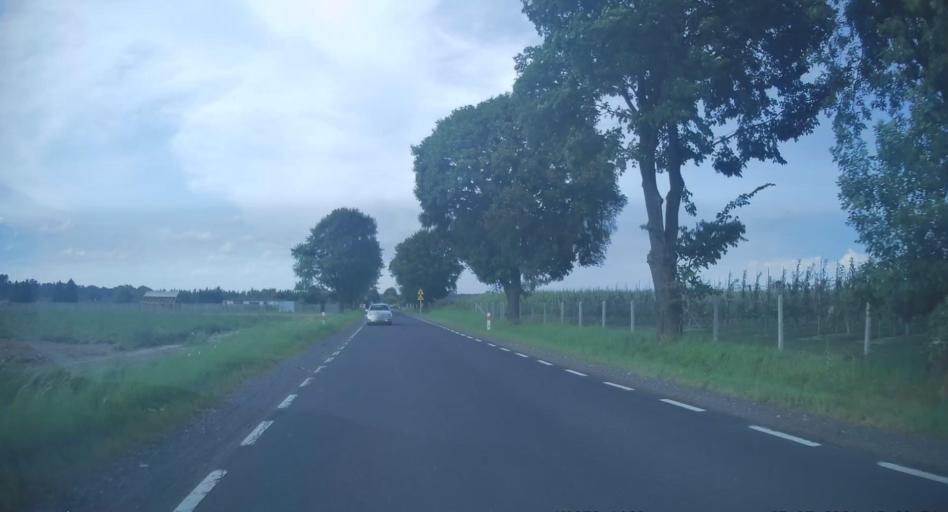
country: PL
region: Lodz Voivodeship
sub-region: Powiat tomaszowski
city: Rzeczyca
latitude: 51.6705
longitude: 20.2642
